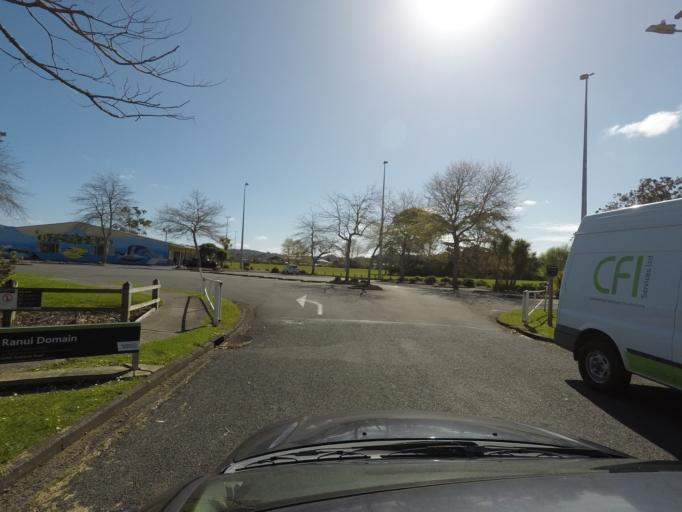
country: NZ
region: Auckland
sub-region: Auckland
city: Rosebank
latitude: -36.8665
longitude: 174.6008
